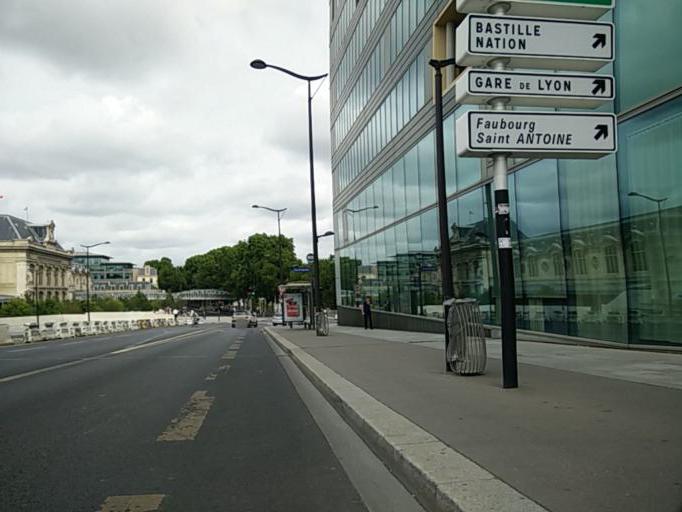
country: FR
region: Ile-de-France
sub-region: Paris
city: Paris
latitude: 48.8413
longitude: 2.3682
